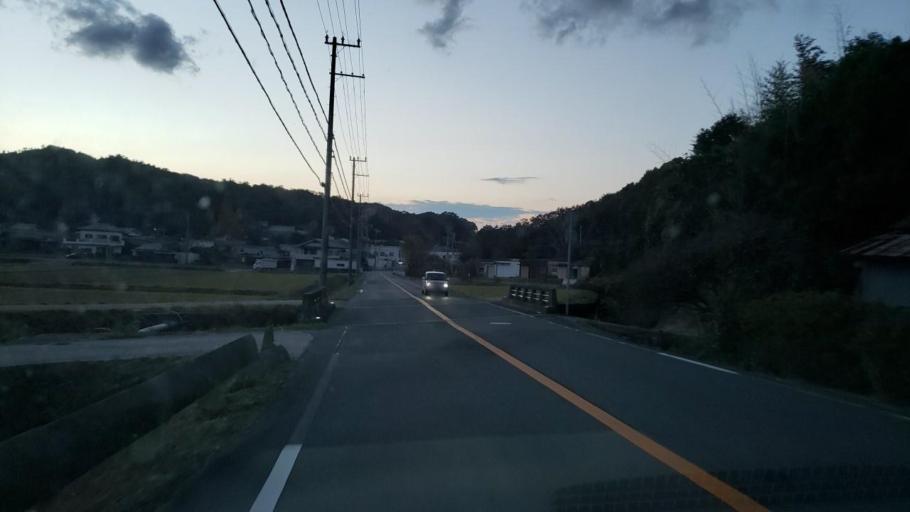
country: JP
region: Hyogo
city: Fukura
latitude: 34.2840
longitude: 134.6917
